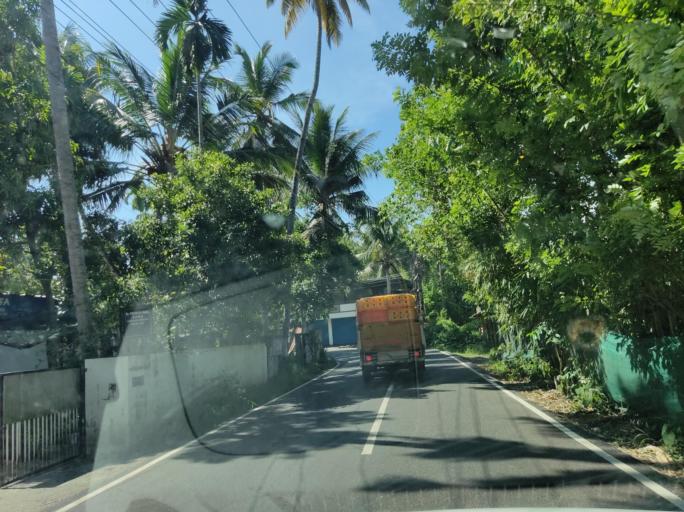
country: IN
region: Kerala
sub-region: Alappuzha
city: Kayankulam
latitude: 9.2665
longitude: 76.4056
